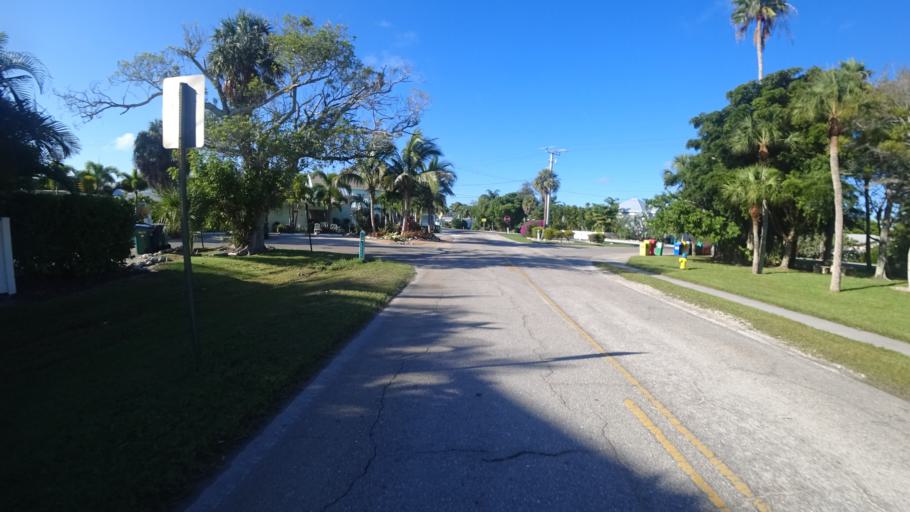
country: US
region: Florida
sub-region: Manatee County
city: Anna Maria
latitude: 27.5200
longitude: -82.7269
